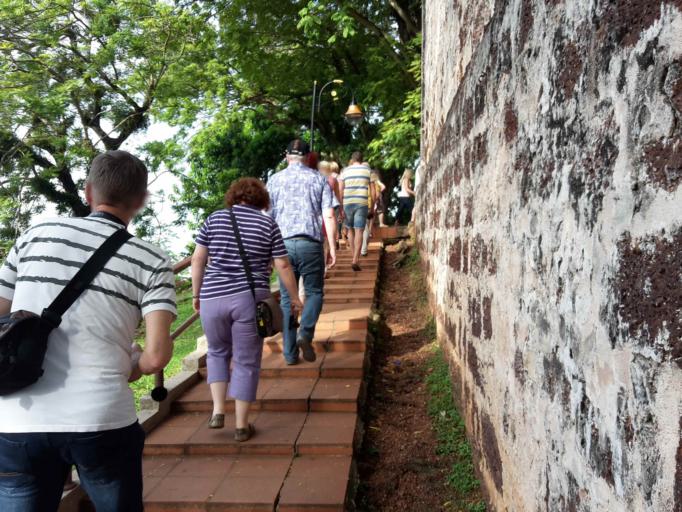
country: MY
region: Melaka
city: Malacca
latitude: 2.1924
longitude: 102.2498
